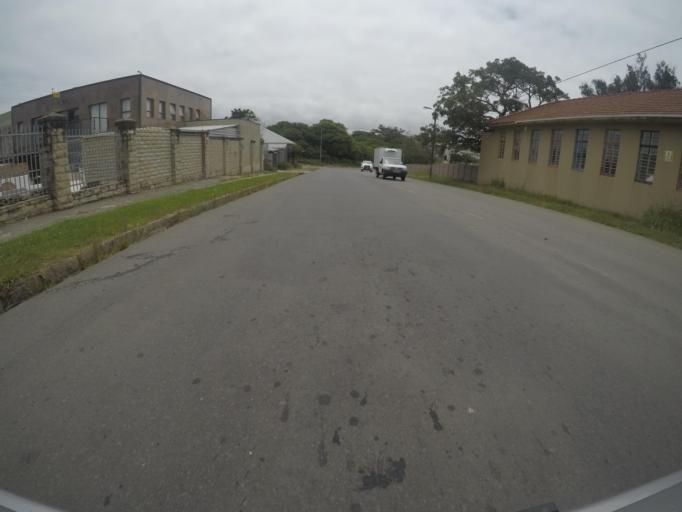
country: ZA
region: Eastern Cape
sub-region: Buffalo City Metropolitan Municipality
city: East London
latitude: -33.0130
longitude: 27.9150
